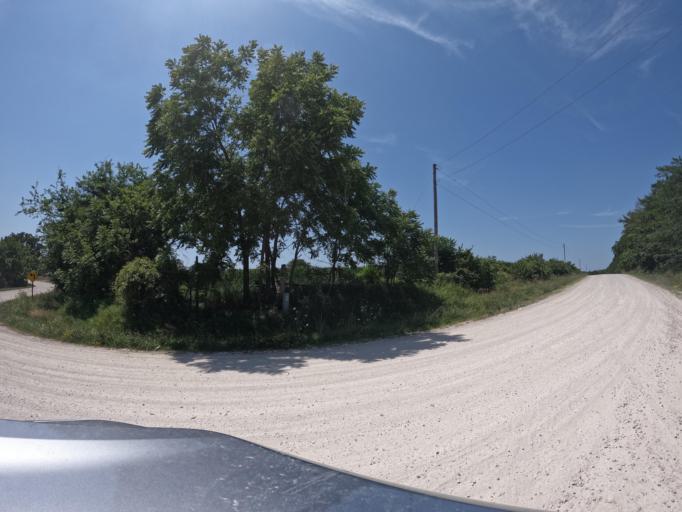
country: US
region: Iowa
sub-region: Henry County
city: Mount Pleasant
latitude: 40.9133
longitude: -91.5504
